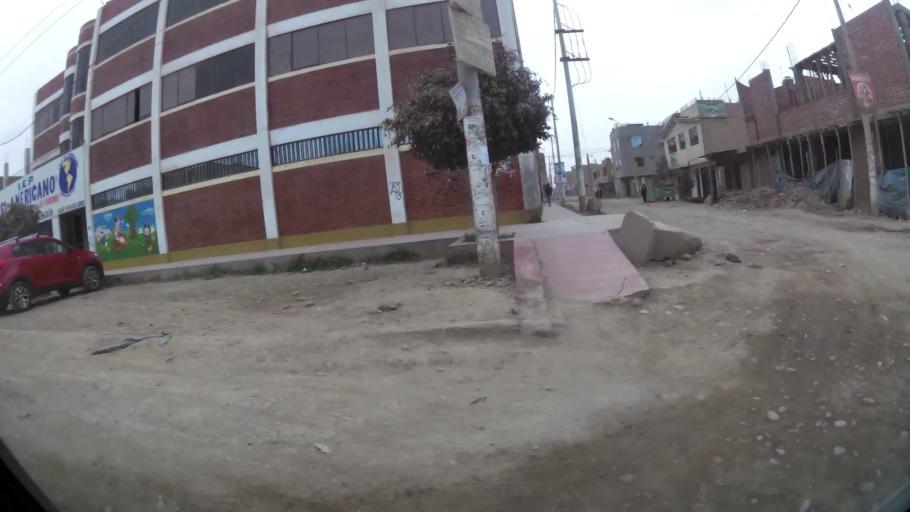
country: PE
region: Lima
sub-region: Lima
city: Independencia
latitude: -11.9583
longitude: -77.0980
